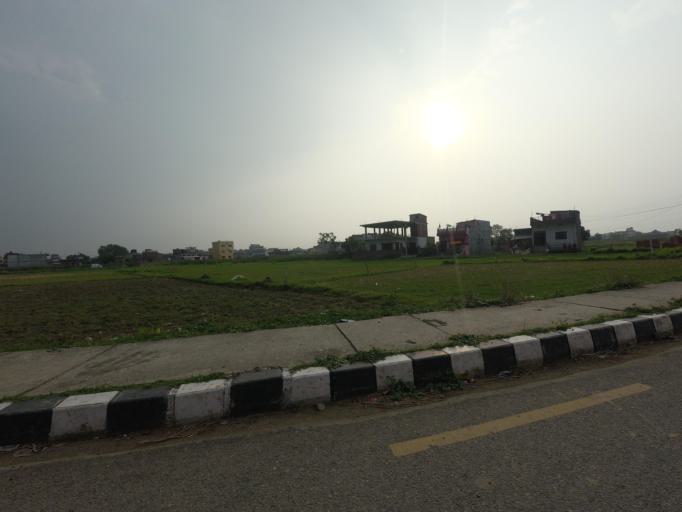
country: NP
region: Western Region
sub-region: Lumbini Zone
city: Bhairahawa
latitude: 27.5039
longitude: 83.4430
